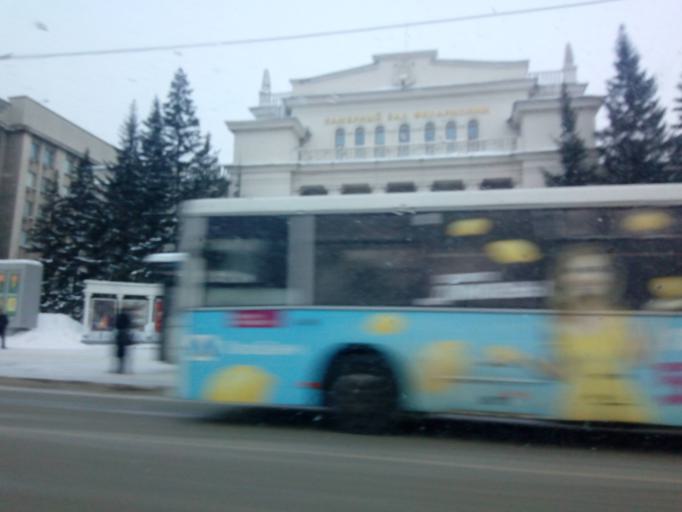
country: RU
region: Novosibirsk
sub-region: Novosibirskiy Rayon
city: Novosibirsk
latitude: 55.0279
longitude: 82.9212
